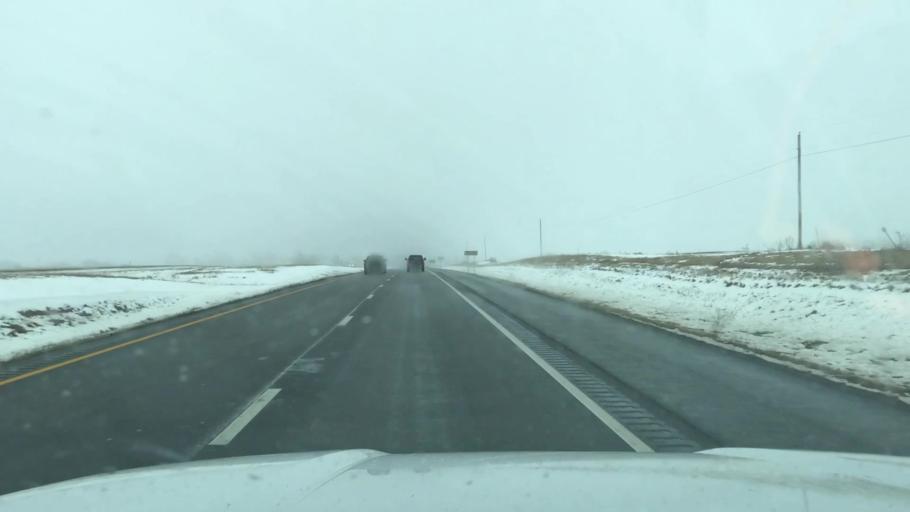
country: US
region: Missouri
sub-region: Clinton County
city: Cameron
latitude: 39.7615
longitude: -94.3664
